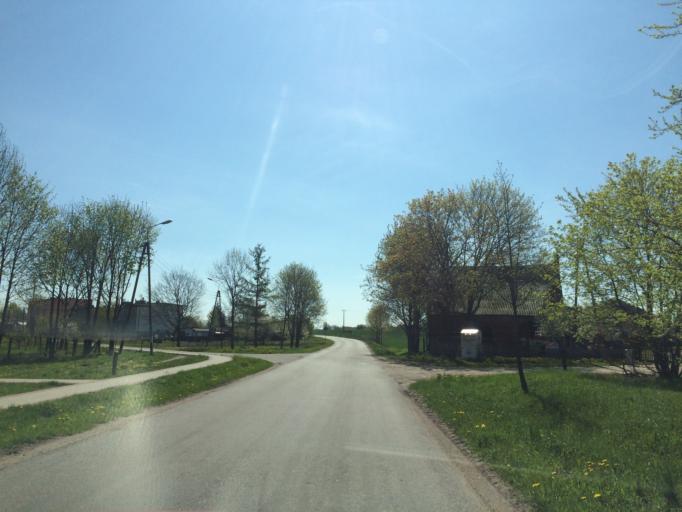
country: PL
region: Warmian-Masurian Voivodeship
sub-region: Powiat dzialdowski
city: Rybno
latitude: 53.3247
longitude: 19.9701
